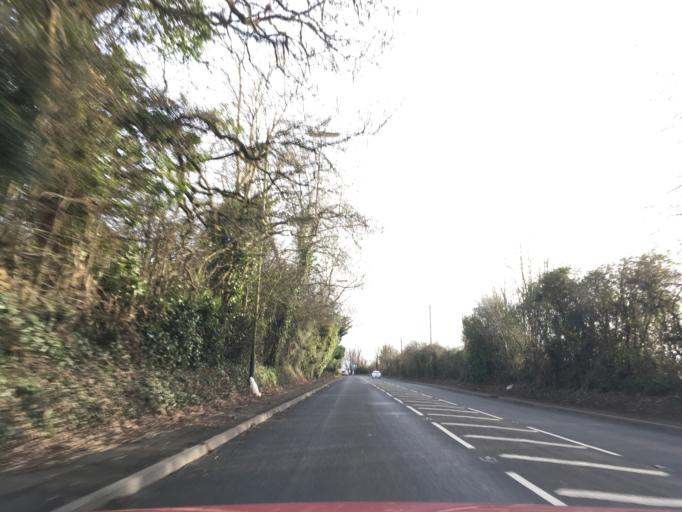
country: GB
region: Wales
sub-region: Caerphilly County Borough
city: Machen
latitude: 51.5926
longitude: -3.1291
